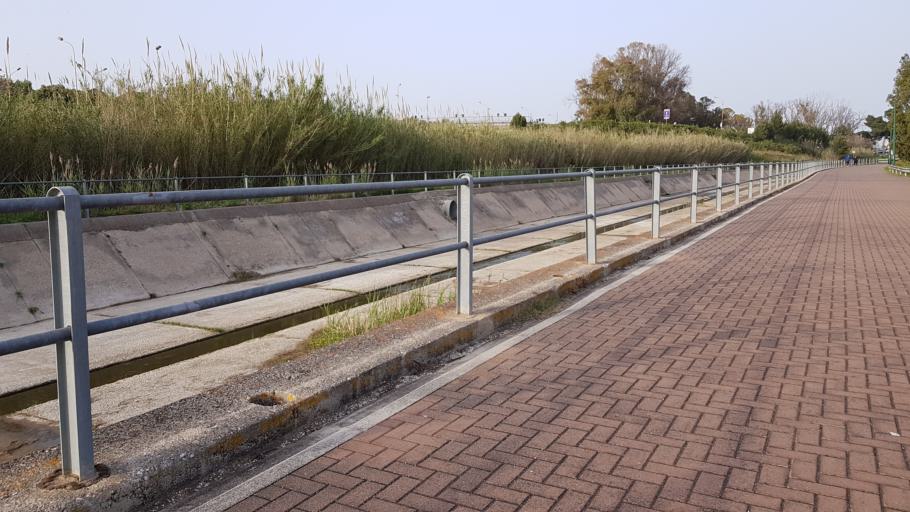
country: IT
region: Apulia
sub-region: Provincia di Brindisi
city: Brindisi
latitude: 40.6395
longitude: 17.9218
